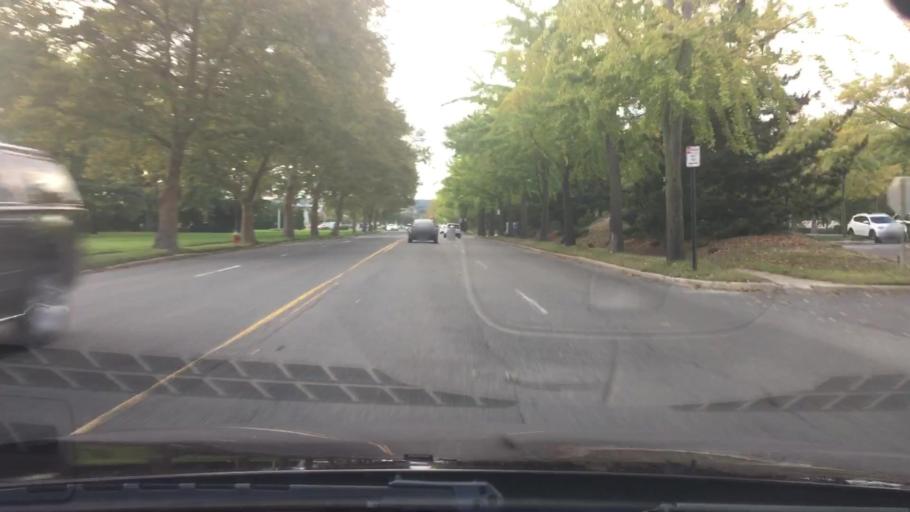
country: US
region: New York
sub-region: Suffolk County
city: Melville
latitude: 40.7708
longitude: -73.4172
